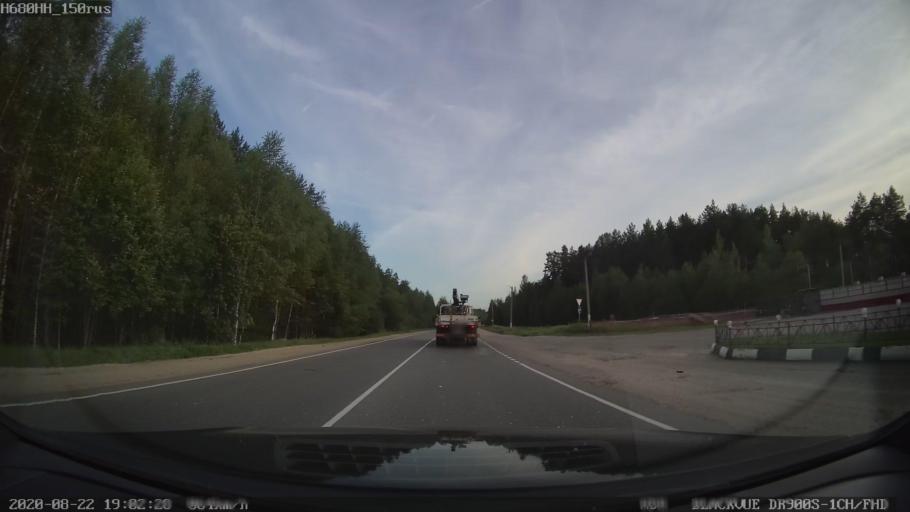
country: RU
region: Tverskaya
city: Sakharovo
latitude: 57.1084
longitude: 36.1201
